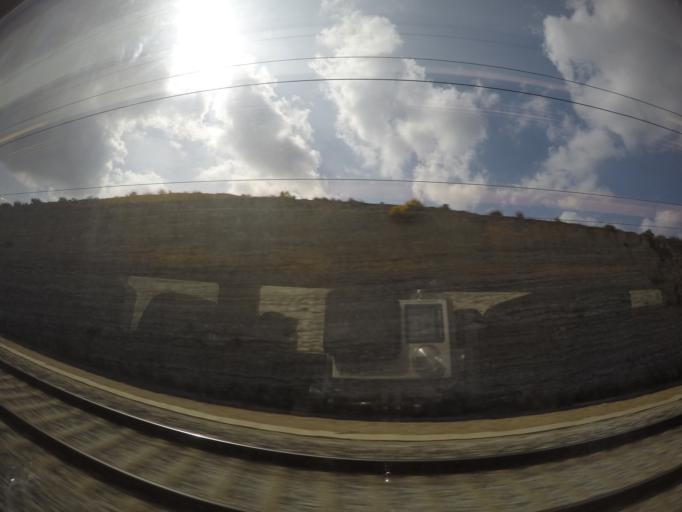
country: ES
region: Aragon
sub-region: Provincia de Zaragoza
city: El Burgo de Ebro
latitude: 41.5196
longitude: -0.7015
